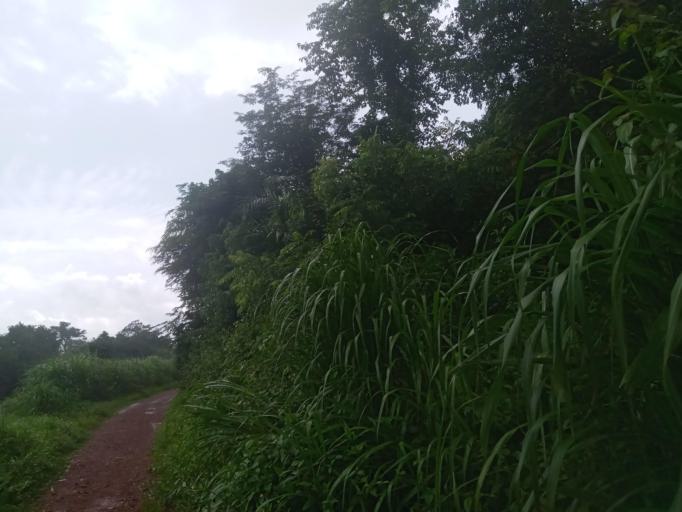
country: SL
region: Northern Province
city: Bumbuna
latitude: 8.9207
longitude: -11.7422
